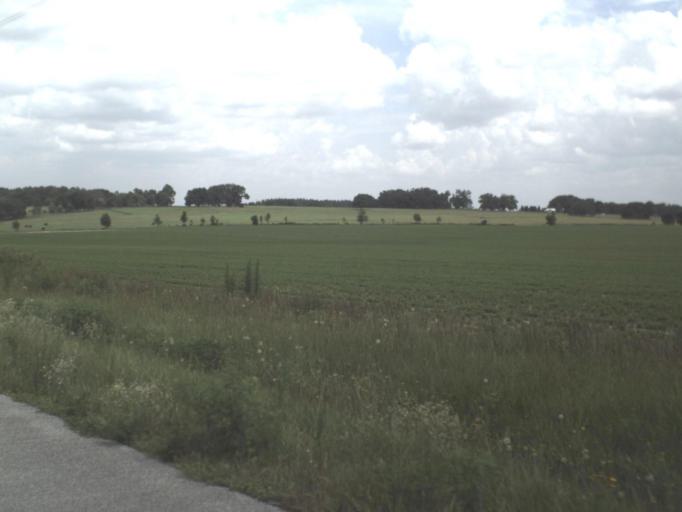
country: US
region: Florida
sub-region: Madison County
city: Madison
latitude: 30.4723
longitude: -83.3213
